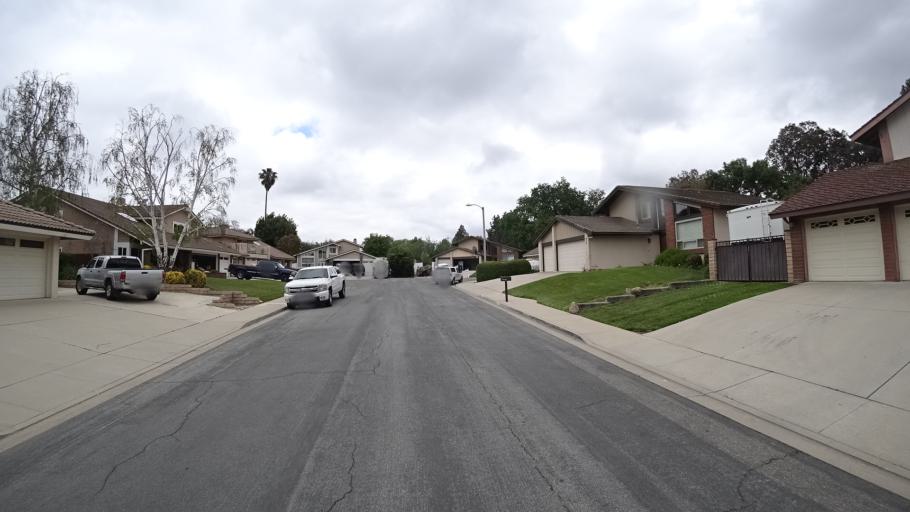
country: US
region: California
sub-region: Ventura County
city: Moorpark
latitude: 34.2239
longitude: -118.8867
